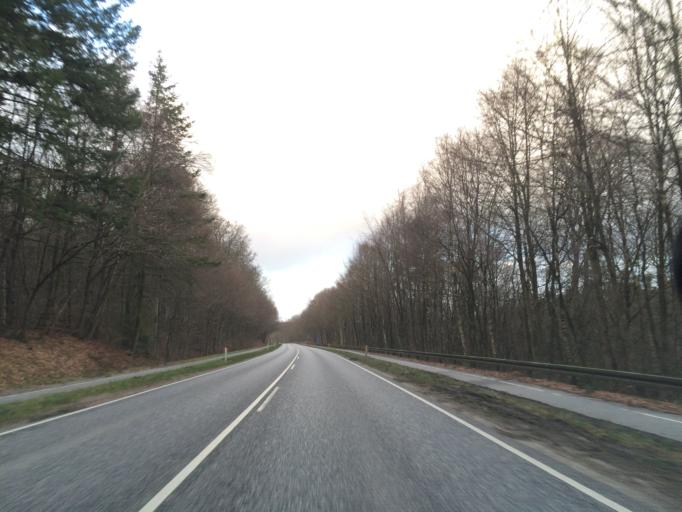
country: DK
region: Central Jutland
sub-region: Silkeborg Kommune
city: Virklund
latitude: 56.1430
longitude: 9.5594
